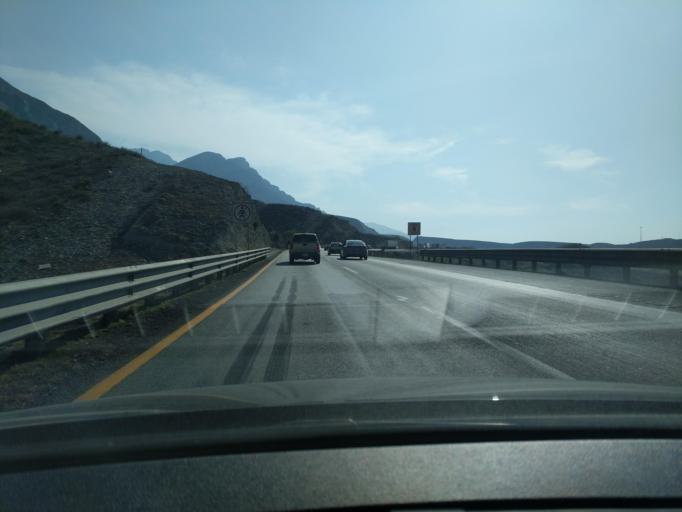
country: MX
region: Nuevo Leon
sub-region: Garcia
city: Las Torres de Guadalupe
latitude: 25.6523
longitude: -100.7279
